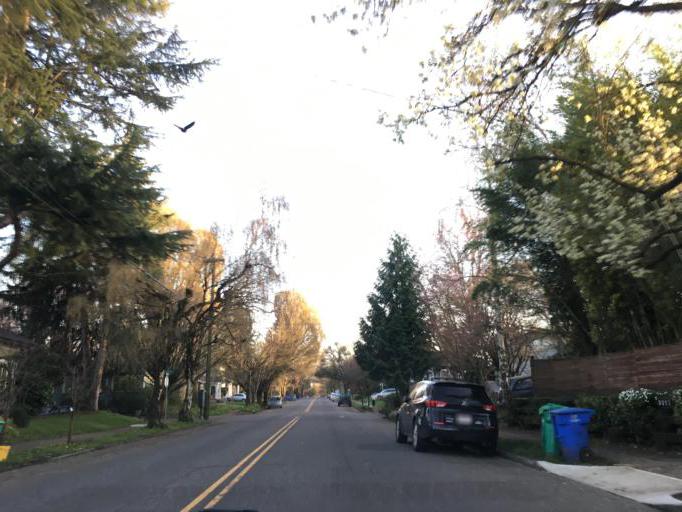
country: US
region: Oregon
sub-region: Multnomah County
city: Portland
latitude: 45.5472
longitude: -122.6504
